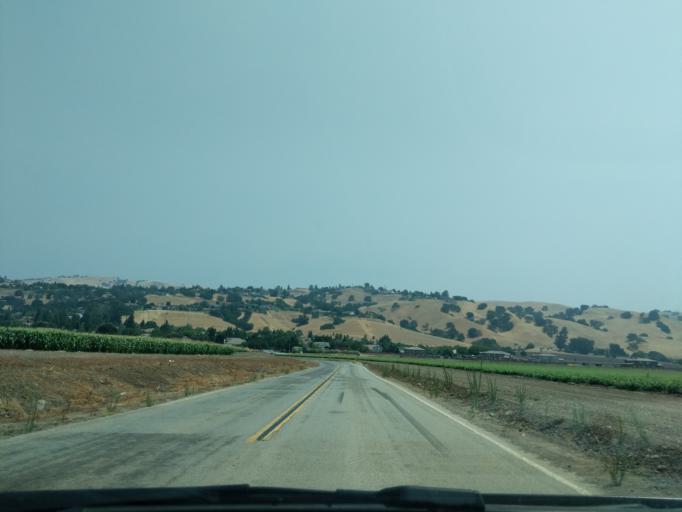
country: US
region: California
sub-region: Santa Clara County
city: San Martin
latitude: 37.1313
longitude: -121.6080
